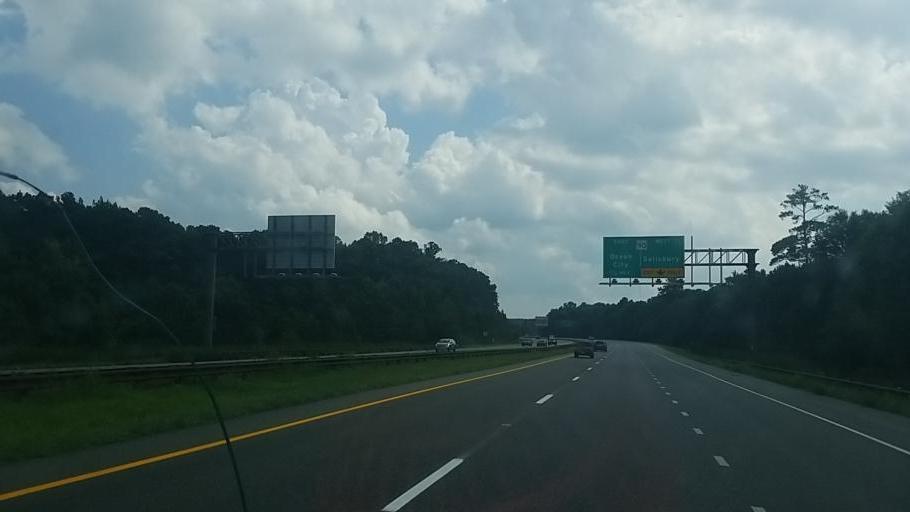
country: US
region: Maryland
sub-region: Worcester County
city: Ocean Pines
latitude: 38.3855
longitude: -75.2048
